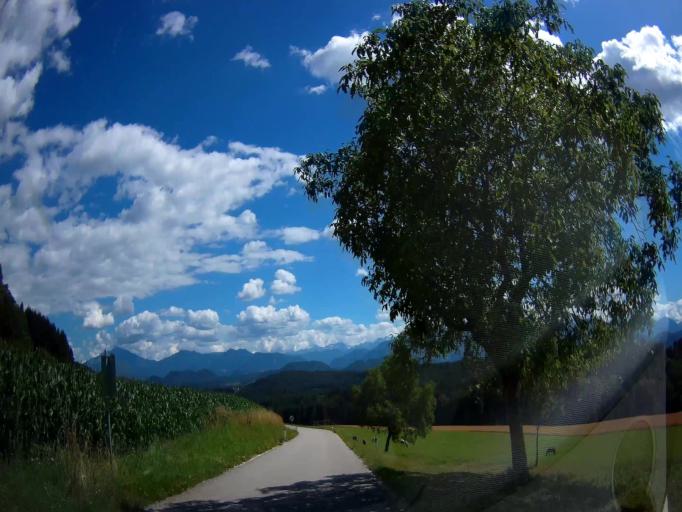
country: AT
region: Carinthia
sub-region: Politischer Bezirk Klagenfurt Land
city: Poggersdorf
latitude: 46.6671
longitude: 14.5326
